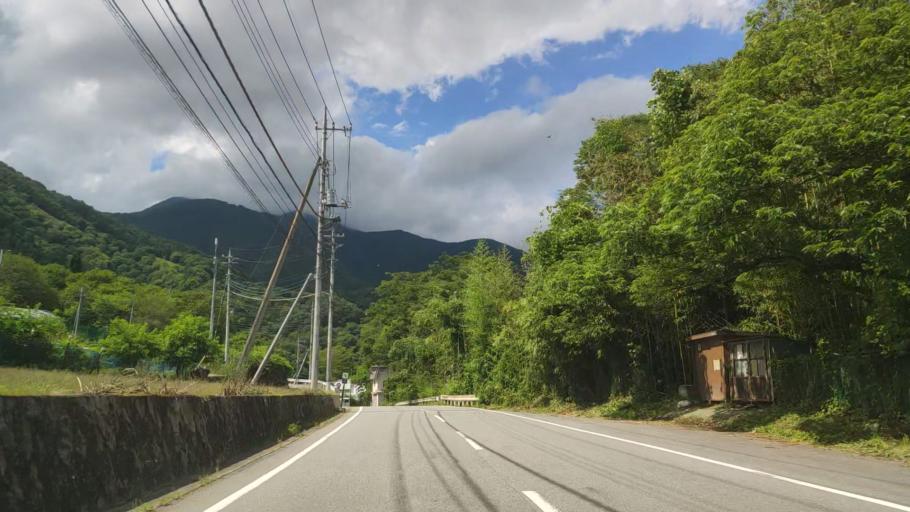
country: JP
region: Yamanashi
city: Enzan
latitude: 35.7831
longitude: 138.7389
